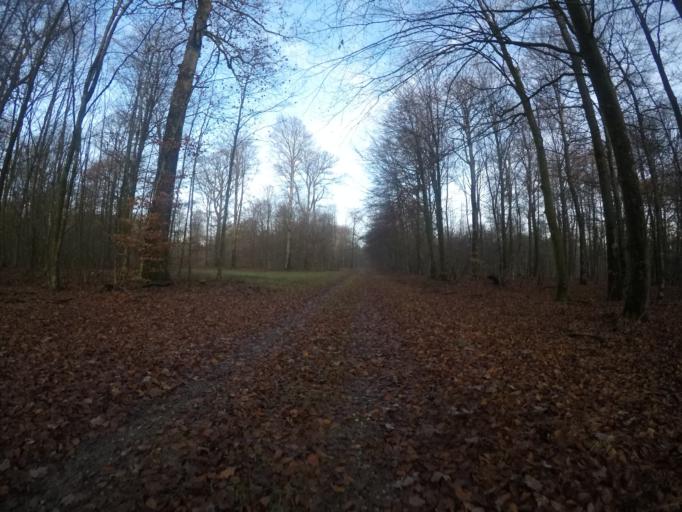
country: BE
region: Wallonia
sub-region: Province du Luxembourg
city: Habay-la-Vieille
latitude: 49.7545
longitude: 5.6698
